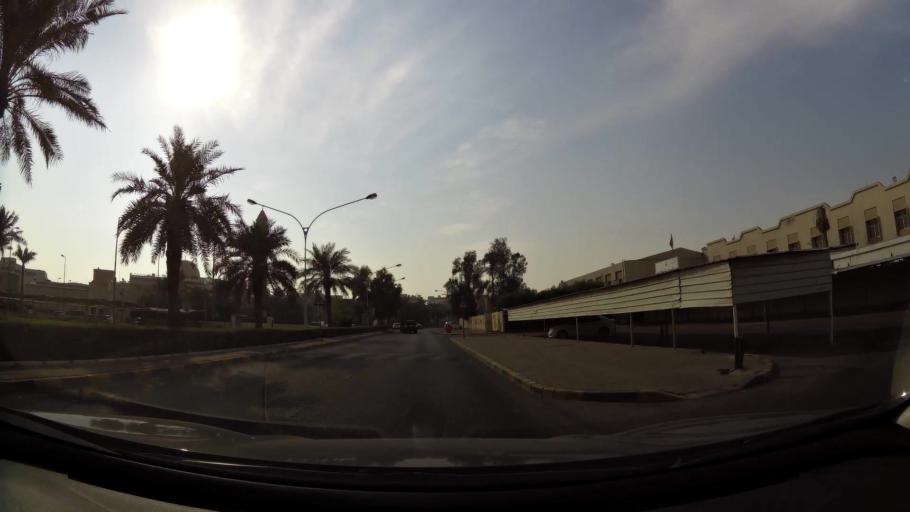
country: KW
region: Al Asimah
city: Ash Shamiyah
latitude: 29.3144
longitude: 47.9853
